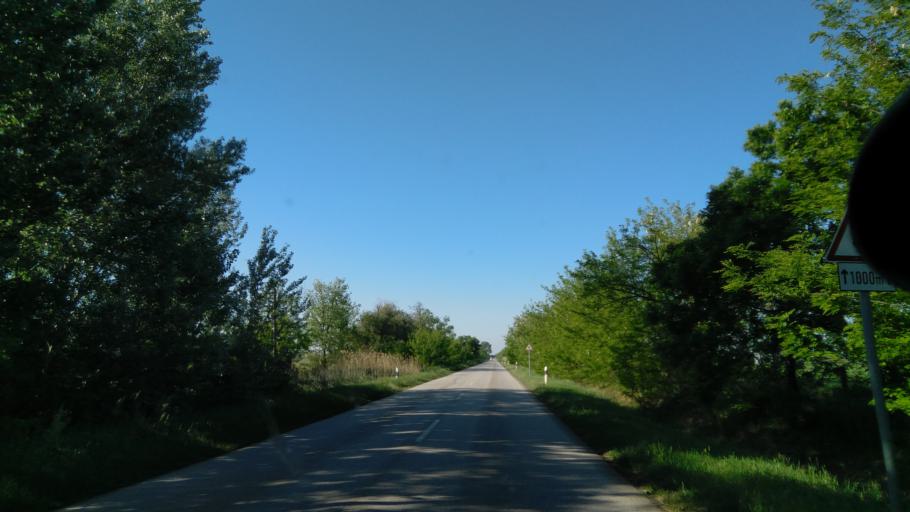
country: HU
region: Bekes
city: Elek
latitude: 46.5557
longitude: 21.2610
